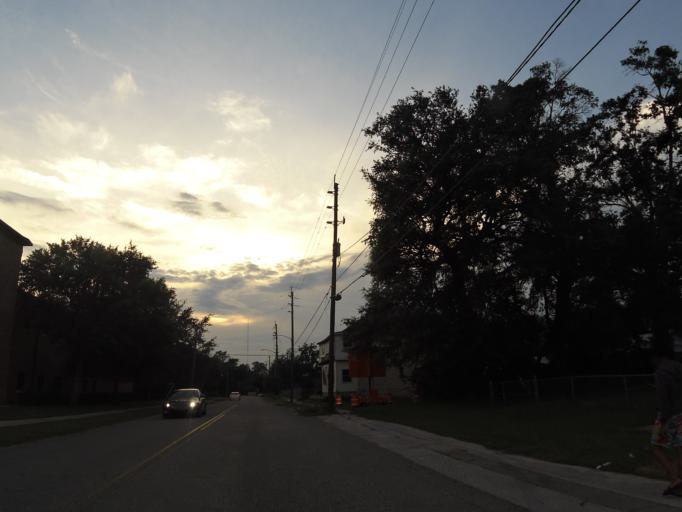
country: US
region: Florida
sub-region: Duval County
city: Jacksonville
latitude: 30.3258
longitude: -81.6868
